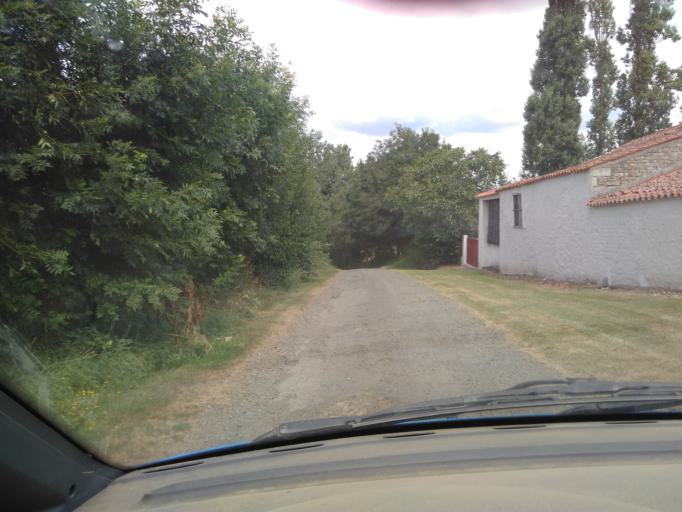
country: FR
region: Pays de la Loire
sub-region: Departement de la Vendee
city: Sainte-Hermine
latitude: 46.5563
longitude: -1.0275
